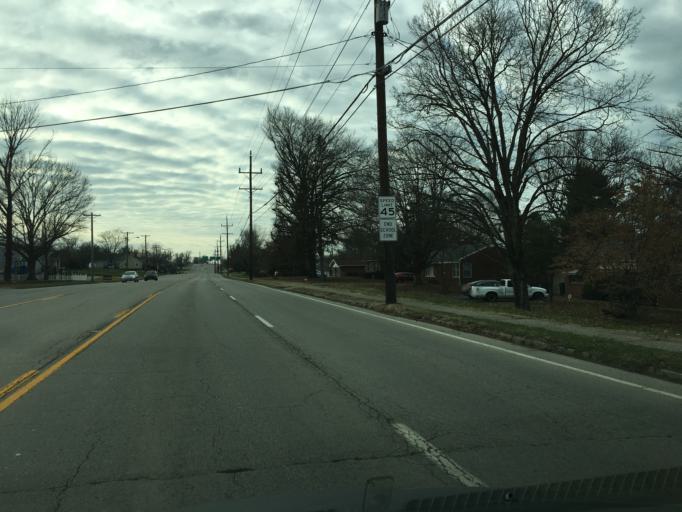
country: US
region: Kentucky
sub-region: Franklin County
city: Frankfort
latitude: 38.2084
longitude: -84.8287
